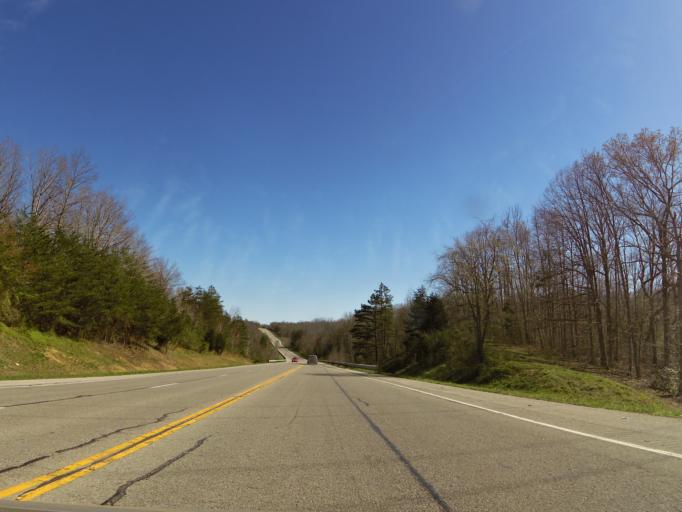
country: US
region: Kentucky
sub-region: McCreary County
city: Stearns
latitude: 36.6869
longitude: -84.4528
